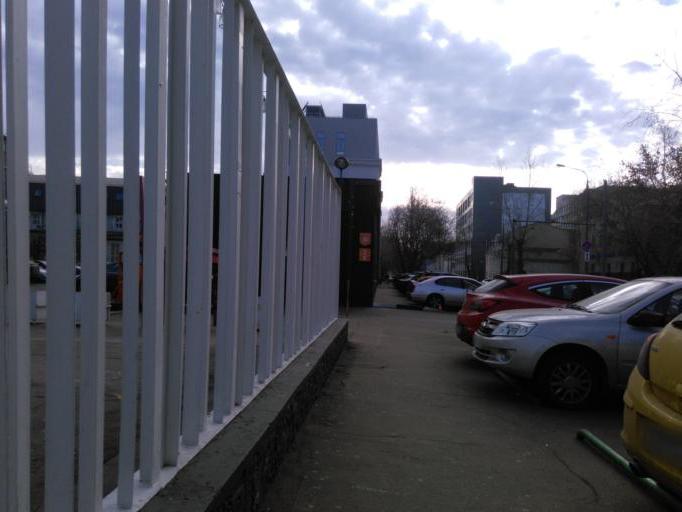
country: RU
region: Moscow
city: Mar'ina Roshcha
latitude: 55.8051
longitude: 37.5844
